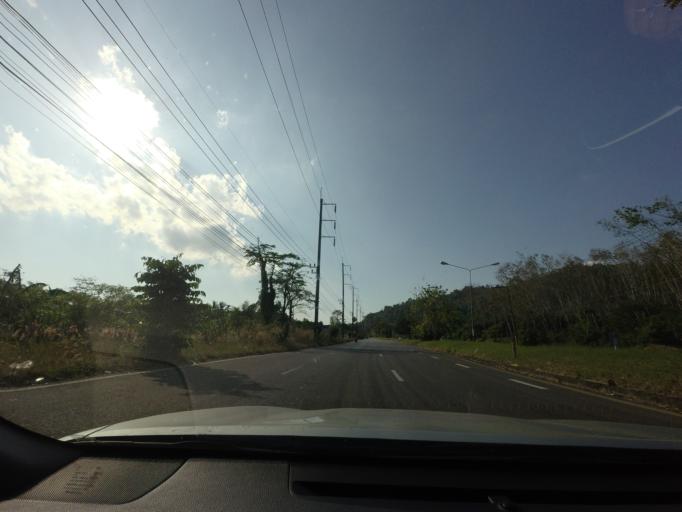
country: TH
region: Phangnga
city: Thai Mueang
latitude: 8.2712
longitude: 98.3289
